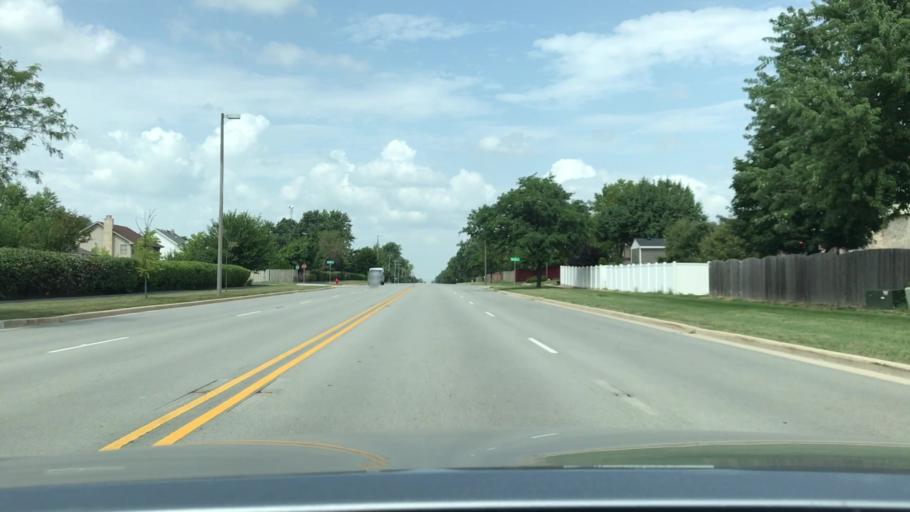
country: US
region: Illinois
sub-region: DuPage County
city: Woodridge
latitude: 41.7413
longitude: -88.0308
